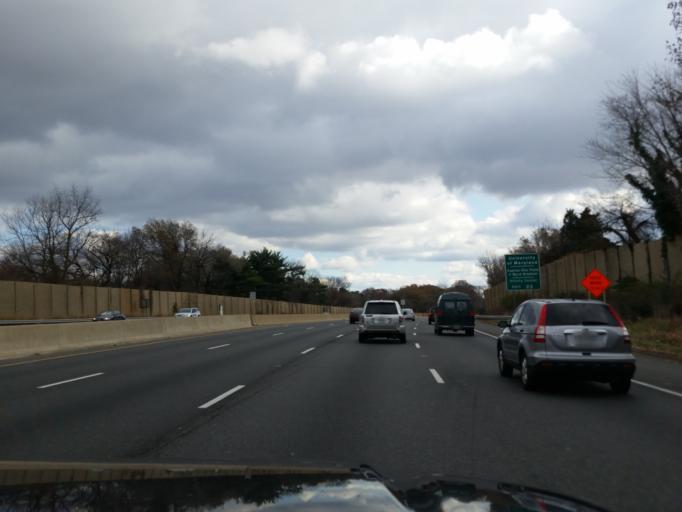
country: US
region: Maryland
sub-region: Prince George's County
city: Beltsville
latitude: 39.0184
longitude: -76.9185
